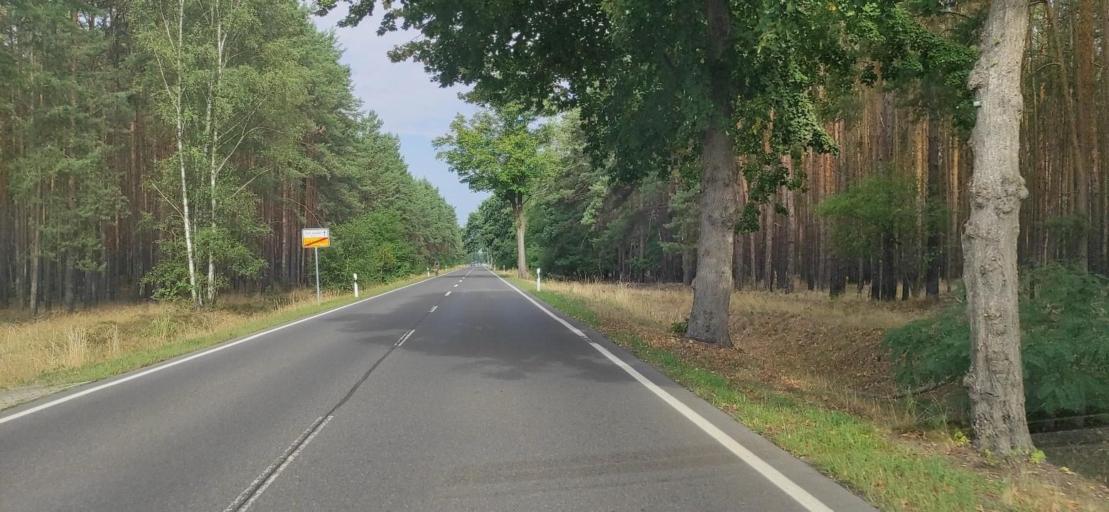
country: DE
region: Brandenburg
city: Forst
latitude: 51.6960
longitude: 14.7064
